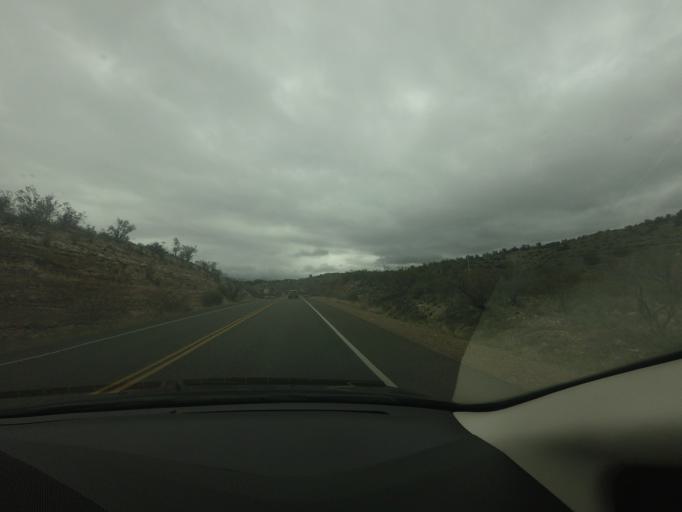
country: US
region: Arizona
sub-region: Yavapai County
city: Lake Montezuma
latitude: 34.6394
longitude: -111.8081
